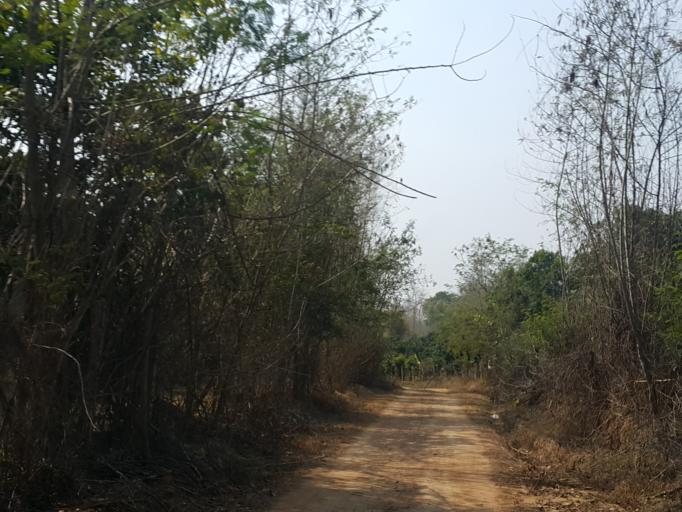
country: TH
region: Chiang Mai
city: Hang Dong
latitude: 18.7285
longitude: 98.8536
